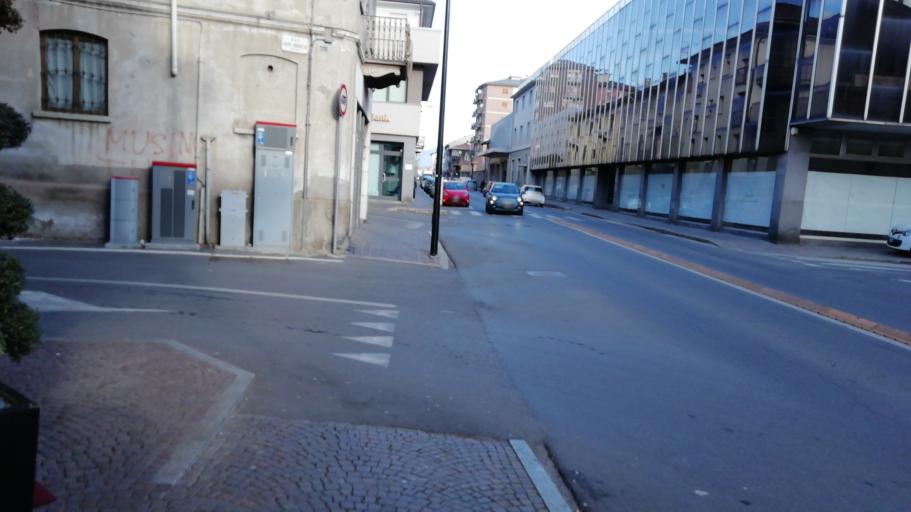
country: IT
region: Piedmont
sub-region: Provincia di Novara
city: Borgomanero
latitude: 45.7029
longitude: 8.4589
